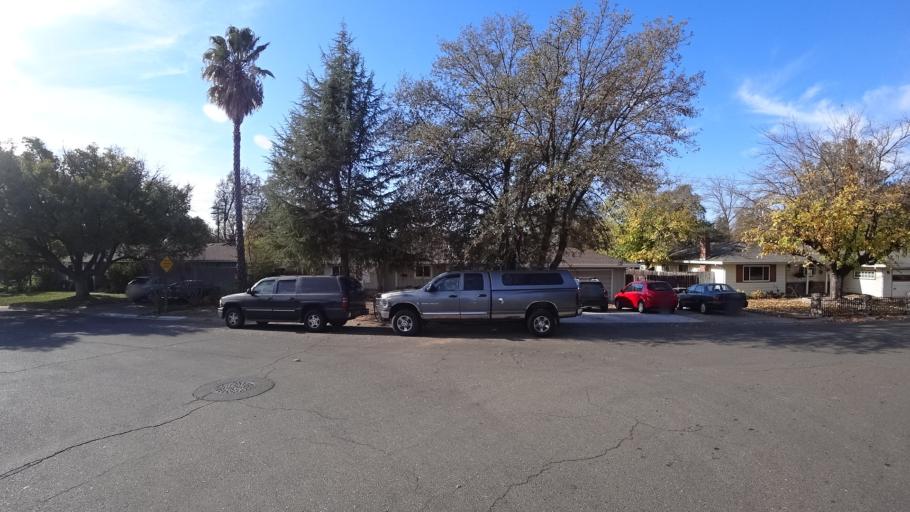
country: US
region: California
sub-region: Sacramento County
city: Fair Oaks
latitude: 38.6695
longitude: -121.2879
